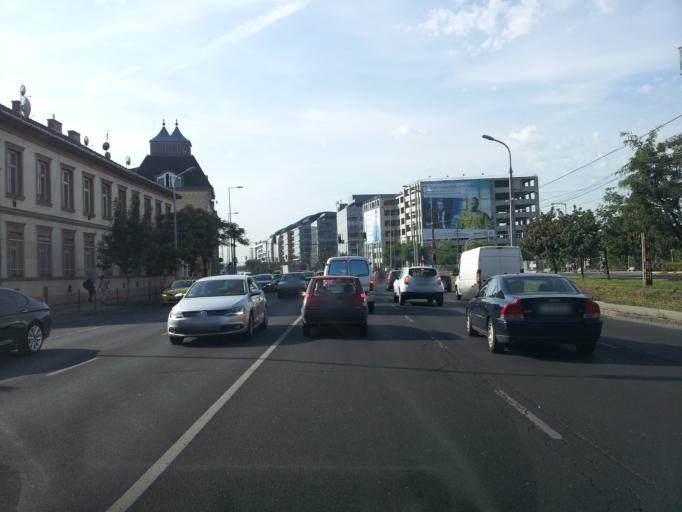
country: HU
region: Budapest
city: Budapest IX. keruelet
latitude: 47.4765
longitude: 19.0692
